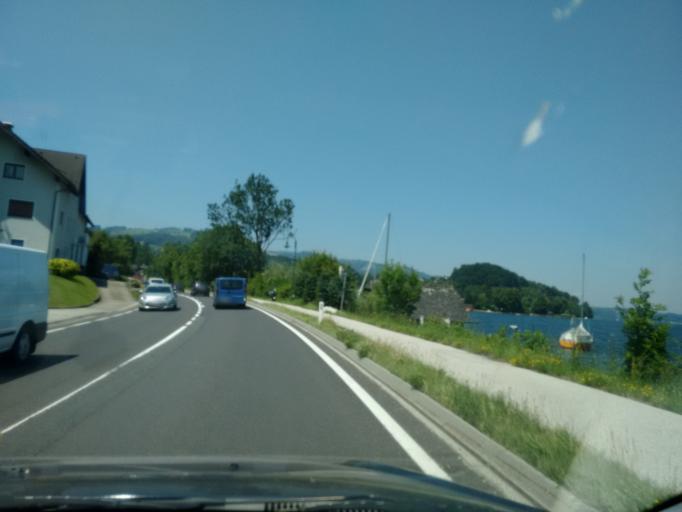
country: AT
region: Upper Austria
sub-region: Politischer Bezirk Gmunden
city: Altmunster
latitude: 47.8618
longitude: 13.7795
